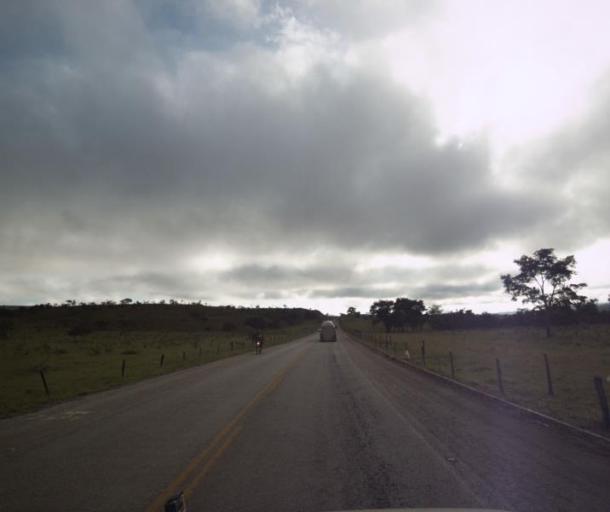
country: BR
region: Goias
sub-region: Pirenopolis
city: Pirenopolis
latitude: -15.7378
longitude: -48.7212
